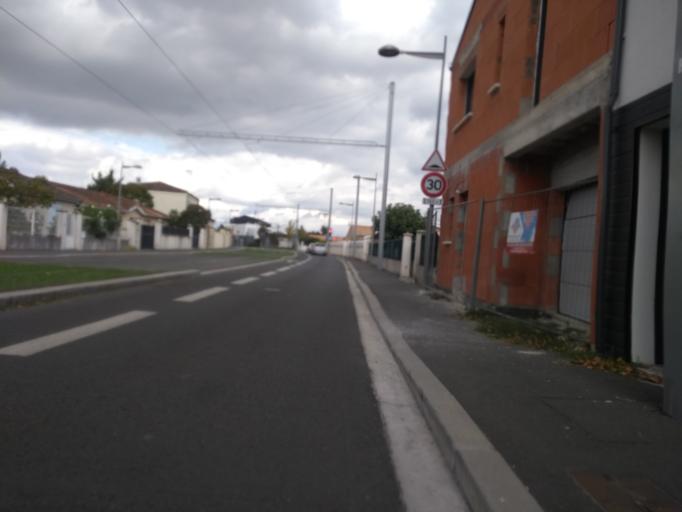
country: FR
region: Aquitaine
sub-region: Departement de la Gironde
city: Begles
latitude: 44.7993
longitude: -0.5513
